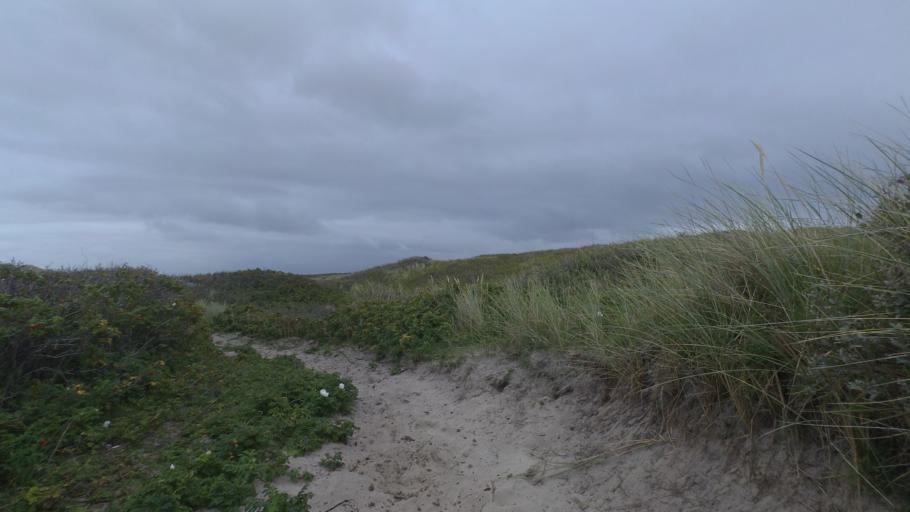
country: NL
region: Friesland
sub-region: Gemeente Ameland
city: Nes
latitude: 53.4600
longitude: 5.7943
